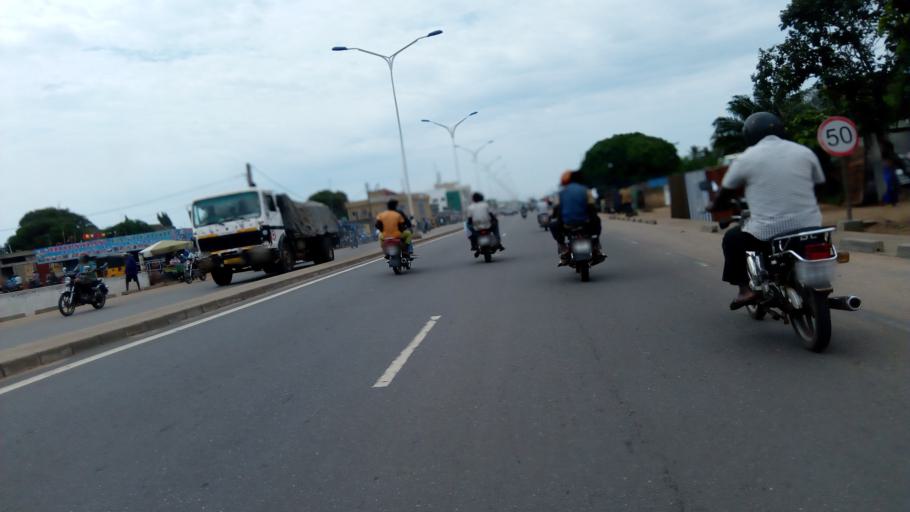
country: TG
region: Maritime
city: Lome
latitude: 6.1646
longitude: 1.2835
